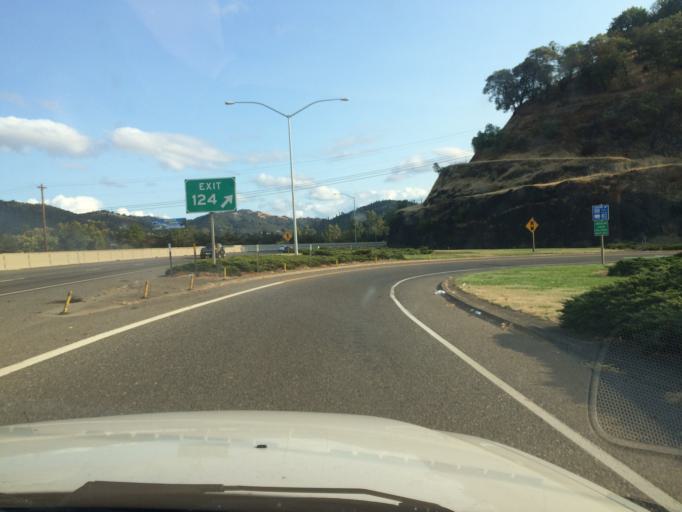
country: US
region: Oregon
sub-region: Douglas County
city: Roseburg
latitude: 43.2136
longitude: -123.3554
